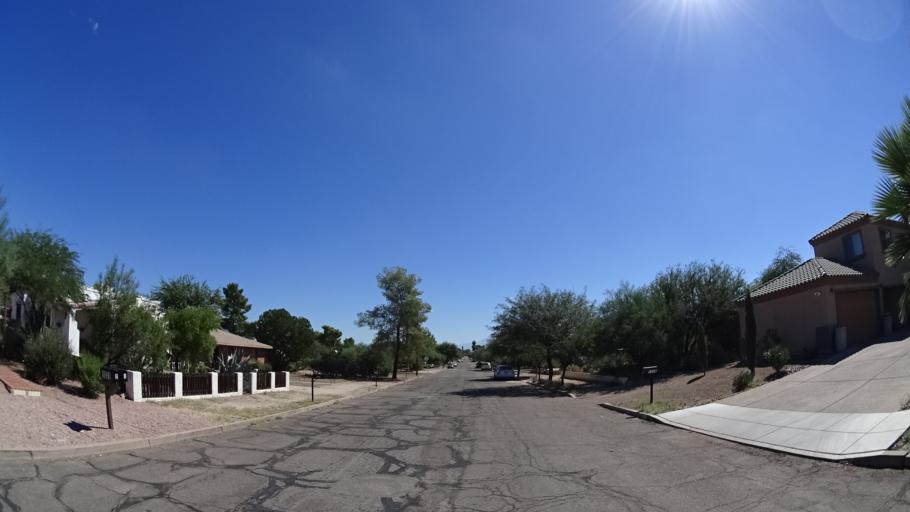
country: US
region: Arizona
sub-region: Pima County
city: Tucson
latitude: 32.2457
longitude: -110.9561
